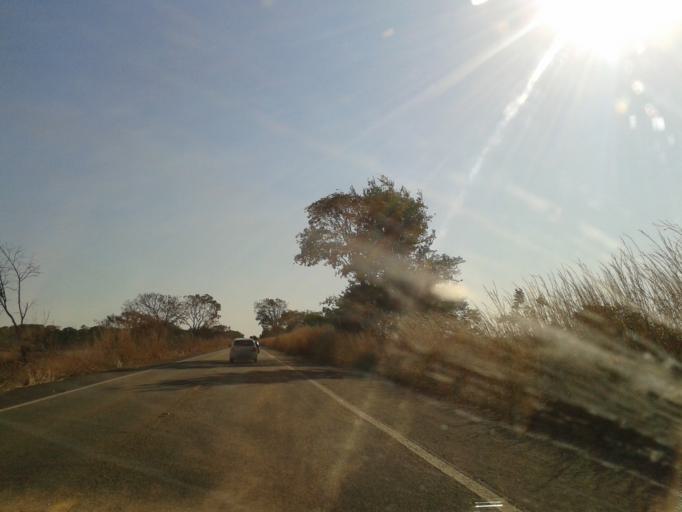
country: BR
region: Goias
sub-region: Mozarlandia
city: Mozarlandia
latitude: -15.0534
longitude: -50.6106
